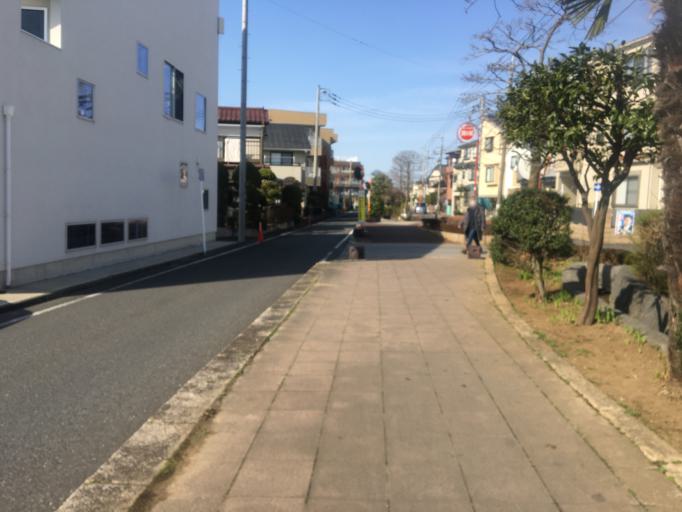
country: JP
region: Saitama
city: Shiki
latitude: 35.8416
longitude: 139.5871
